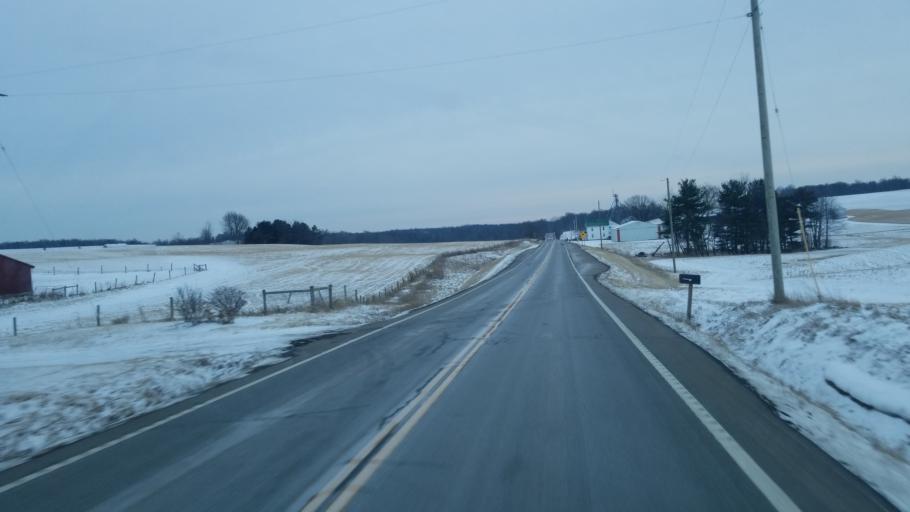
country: US
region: Ohio
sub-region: Ashland County
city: Loudonville
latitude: 40.7298
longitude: -82.2410
